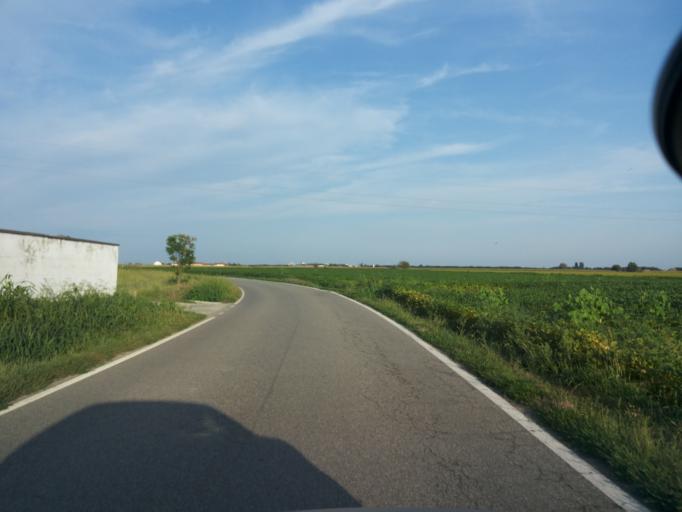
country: IT
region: Piedmont
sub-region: Provincia di Vercelli
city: Tronzano Vercellese
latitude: 45.3384
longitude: 8.1846
